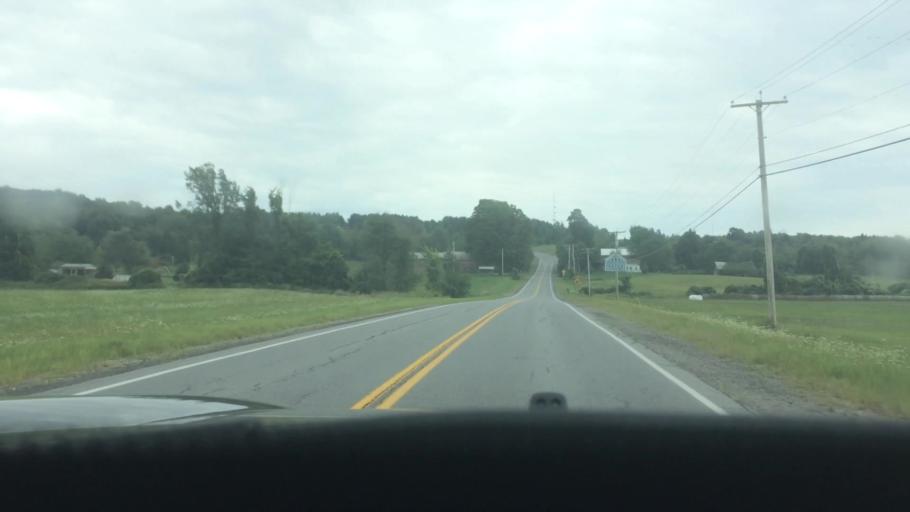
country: US
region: New York
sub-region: St. Lawrence County
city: Canton
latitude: 44.5468
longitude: -75.1032
